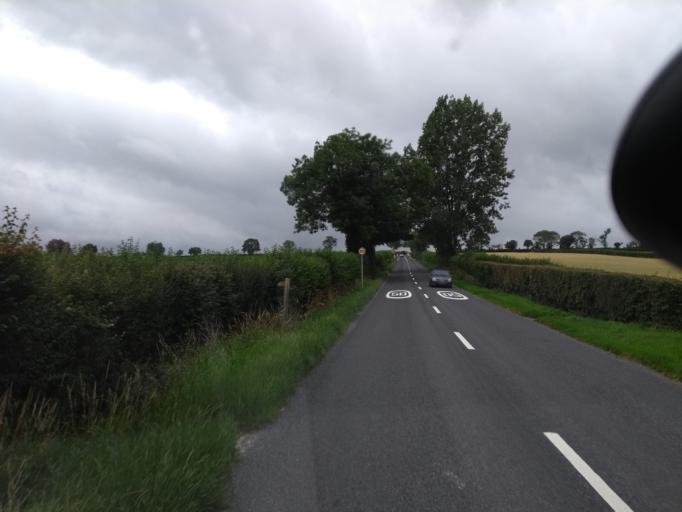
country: GB
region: England
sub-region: Somerset
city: Merriott
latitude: 50.9265
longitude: -2.7694
